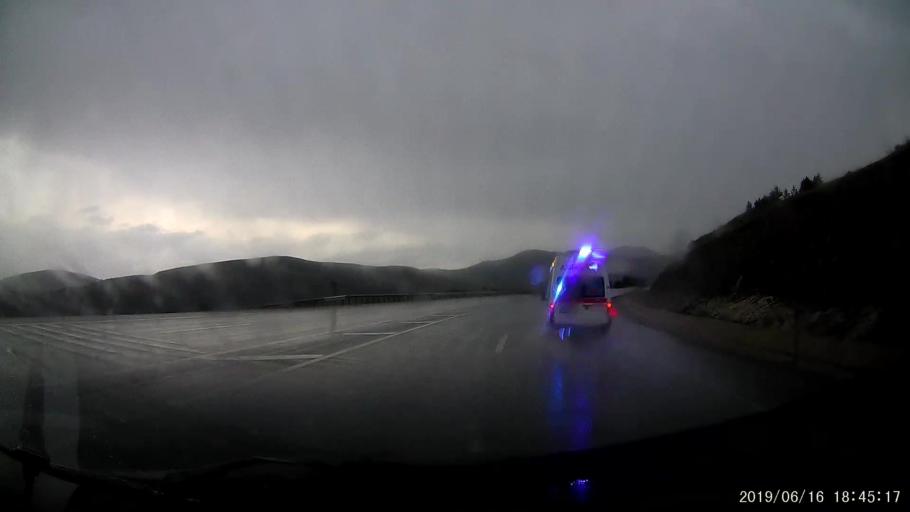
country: TR
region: Erzincan
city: Doganbeyli
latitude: 39.8707
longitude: 39.0599
